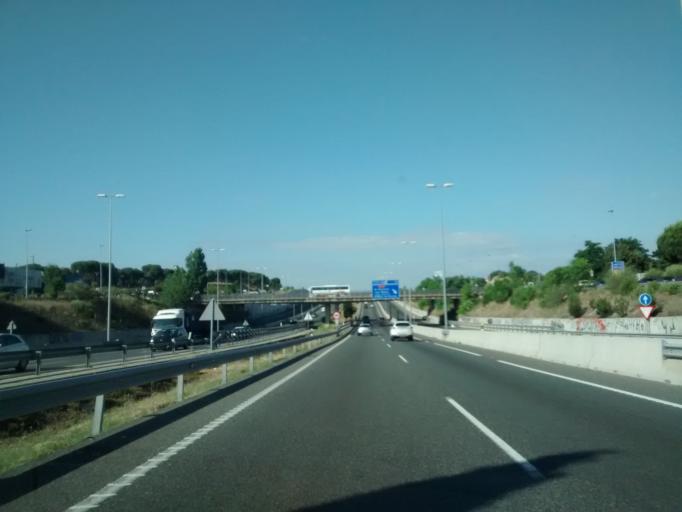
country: ES
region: Madrid
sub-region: Provincia de Madrid
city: Las Rozas de Madrid
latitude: 40.5188
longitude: -3.8901
